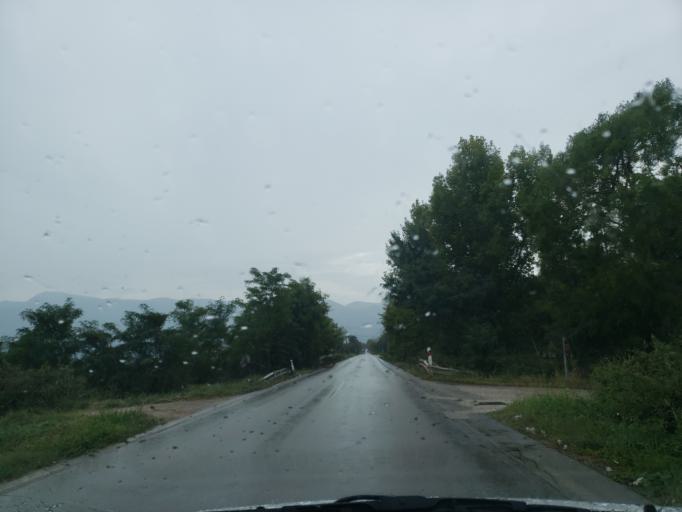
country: GR
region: Central Greece
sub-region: Nomos Fthiotidos
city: Anthili
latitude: 38.8357
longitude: 22.4412
